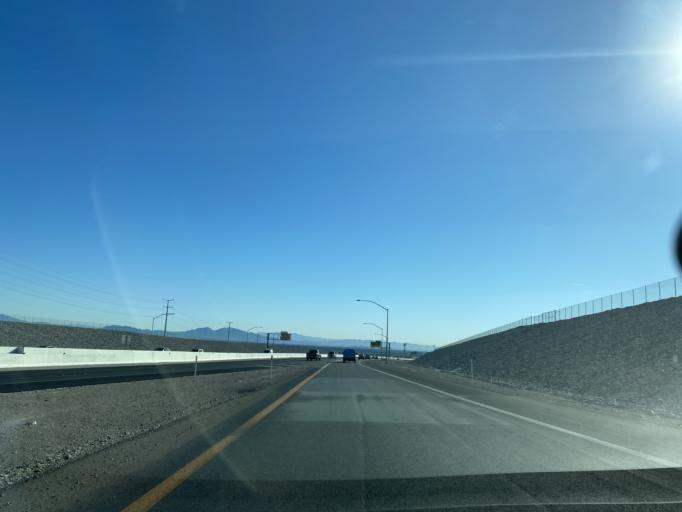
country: US
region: Nevada
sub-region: Clark County
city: Summerlin South
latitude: 36.2592
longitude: -115.3258
